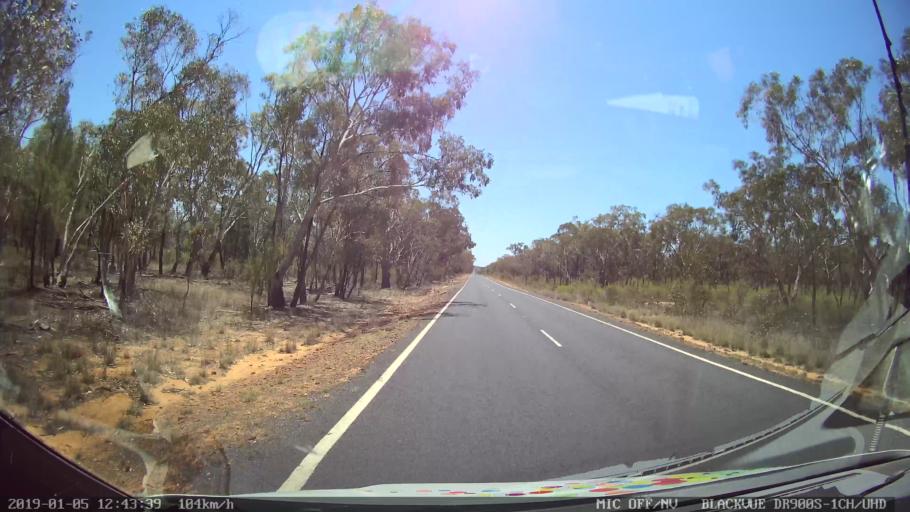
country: AU
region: New South Wales
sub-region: Warrumbungle Shire
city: Coonabarabran
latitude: -31.1459
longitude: 149.5268
